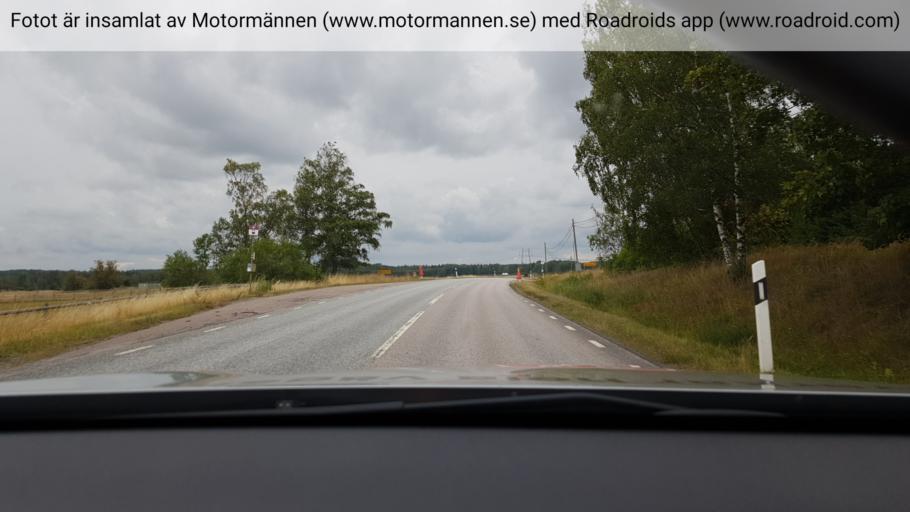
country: SE
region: Stockholm
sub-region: Vallentuna Kommun
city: Vallentuna
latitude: 59.6575
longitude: 18.0431
